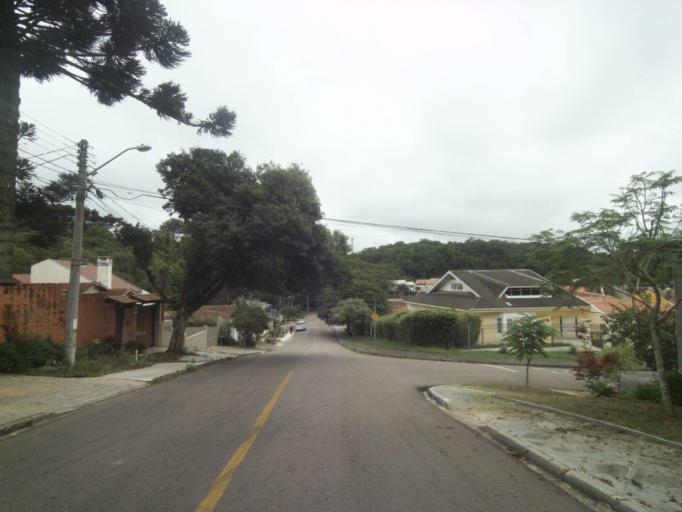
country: BR
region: Parana
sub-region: Curitiba
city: Curitiba
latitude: -25.3994
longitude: -49.2762
